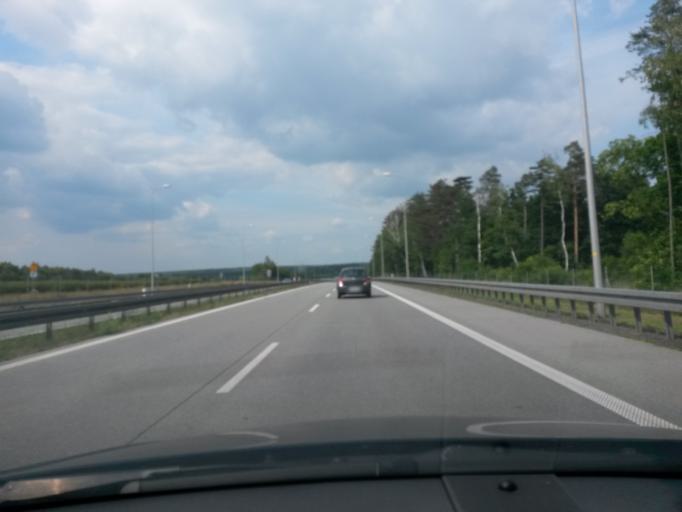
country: PL
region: Lodz Voivodeship
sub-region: Powiat rawski
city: Rawa Mazowiecka
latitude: 51.8200
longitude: 20.3181
